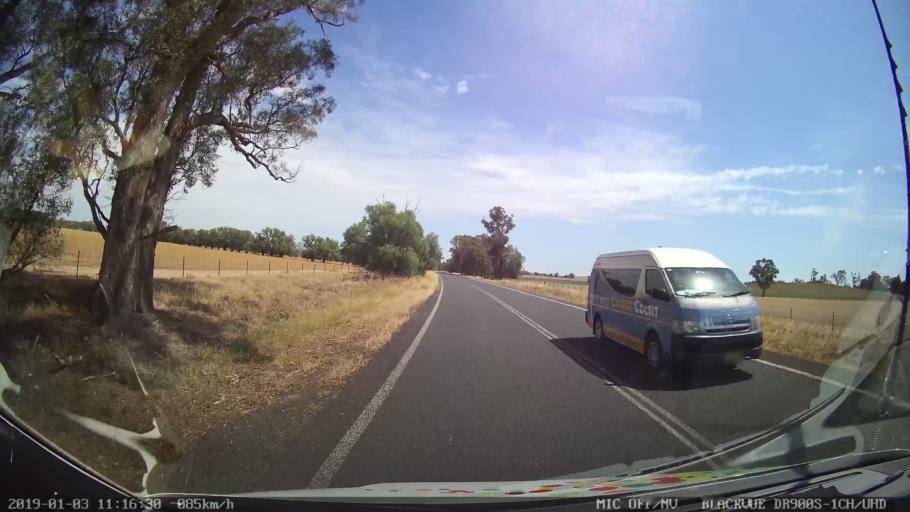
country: AU
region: New South Wales
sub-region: Young
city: Young
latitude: -34.1509
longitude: 148.2697
